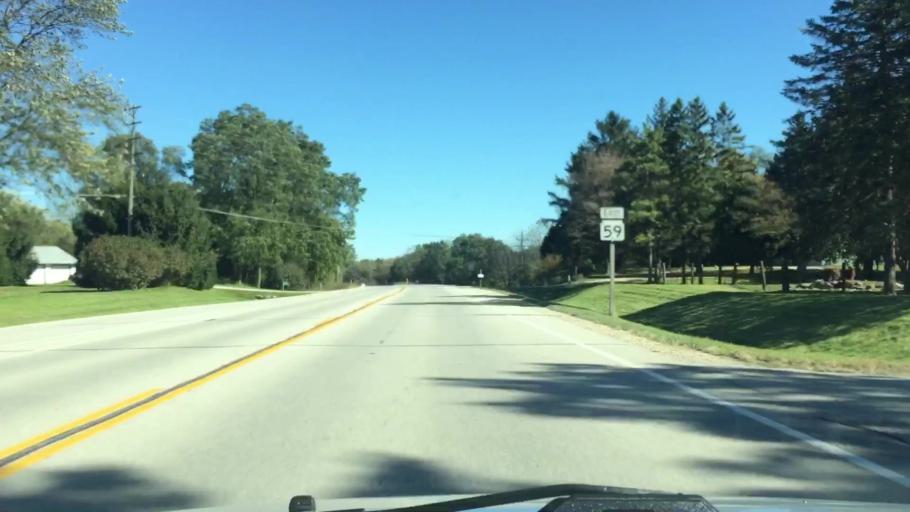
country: US
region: Wisconsin
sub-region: Waukesha County
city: North Prairie
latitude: 42.9443
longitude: -88.3767
